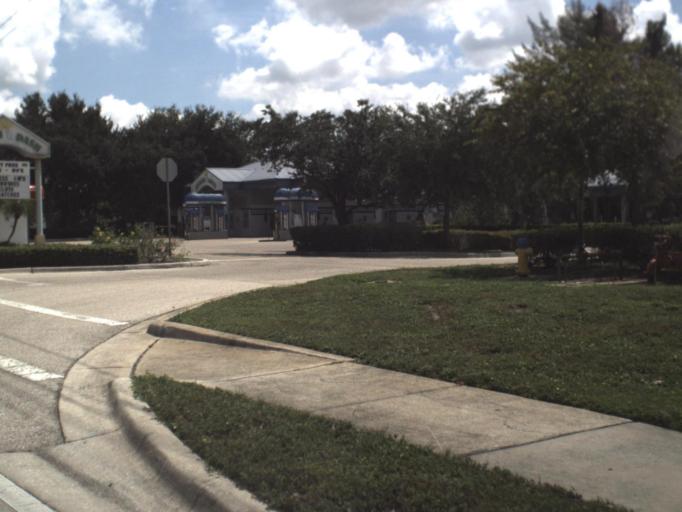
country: US
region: Florida
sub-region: Manatee County
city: West Bradenton
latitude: 27.4626
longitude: -82.6318
